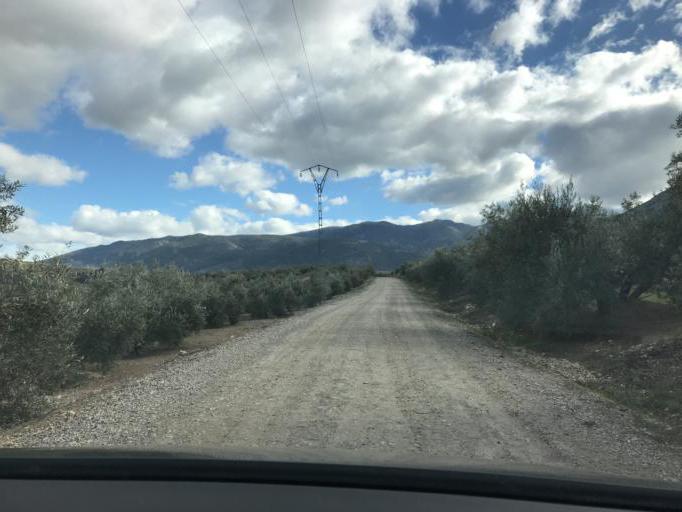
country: ES
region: Andalusia
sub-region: Provincia de Jaen
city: Jimena
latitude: 37.8142
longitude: -3.4325
